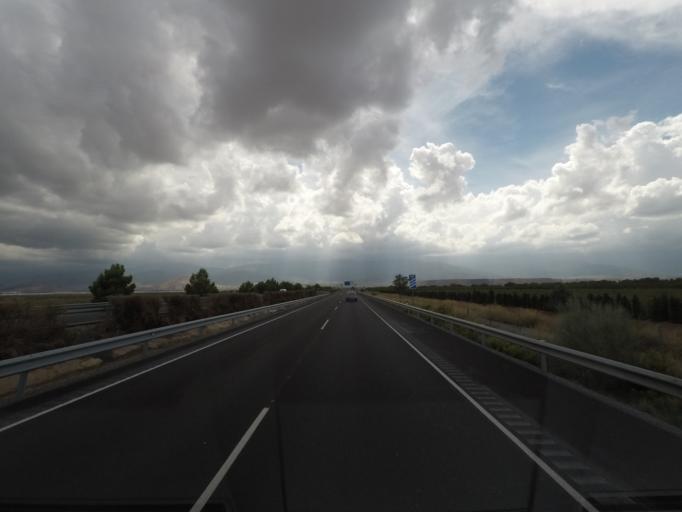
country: ES
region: Andalusia
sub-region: Provincia de Granada
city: Albunan
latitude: 37.2384
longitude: -3.0821
